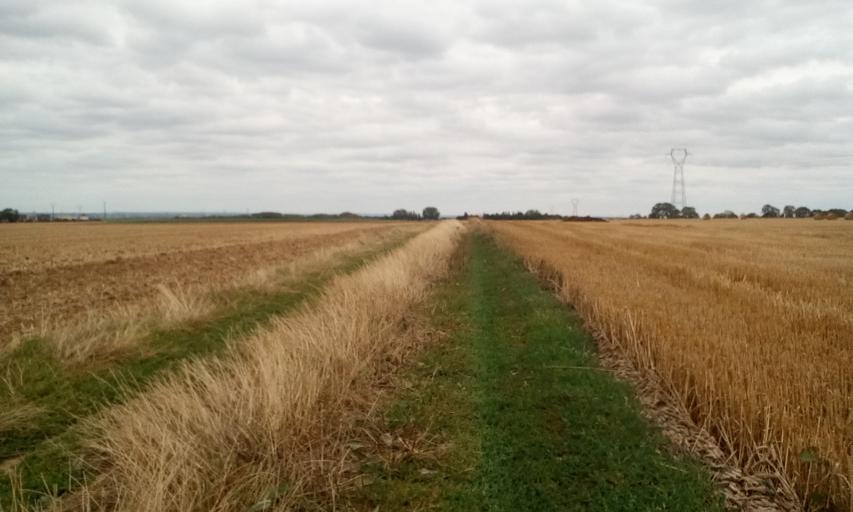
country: FR
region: Lower Normandy
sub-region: Departement du Calvados
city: Fontaine-Etoupefour
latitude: 49.1351
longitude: -0.4584
